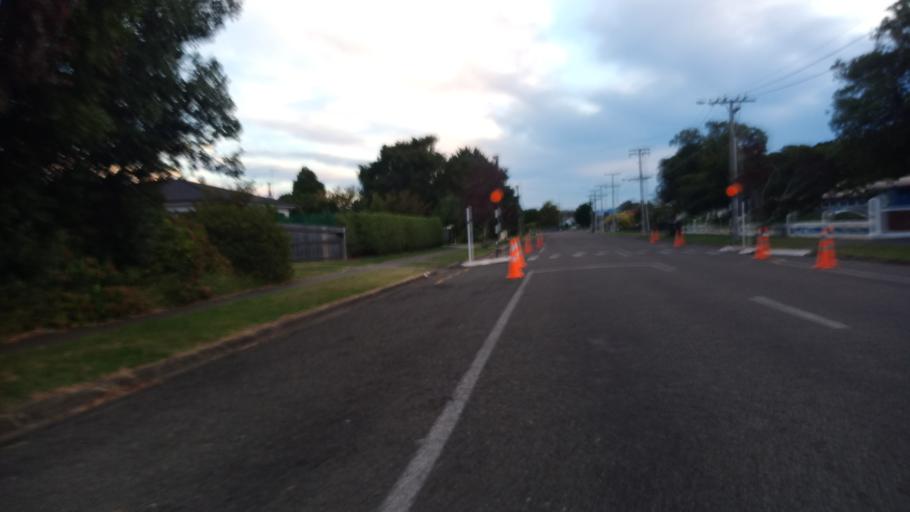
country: NZ
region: Gisborne
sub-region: Gisborne District
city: Gisborne
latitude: -38.6510
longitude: 178.0018
